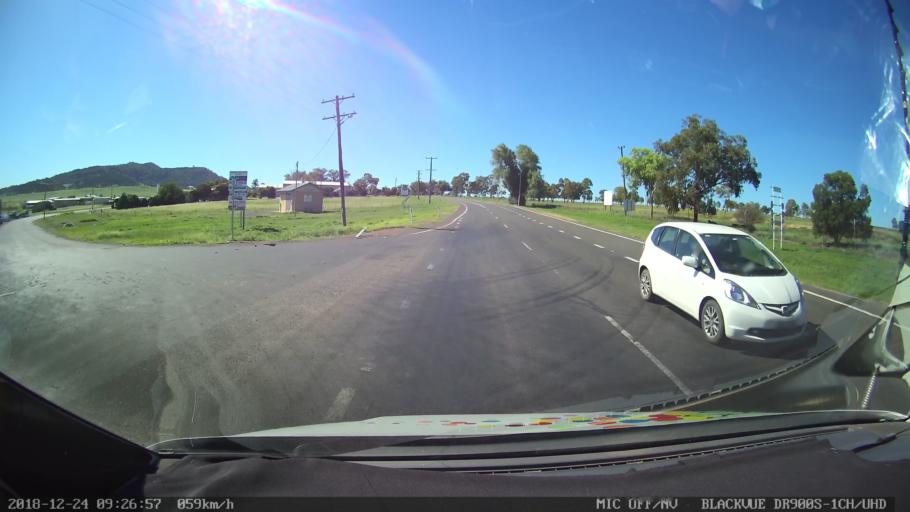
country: AU
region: New South Wales
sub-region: Liverpool Plains
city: Quirindi
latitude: -31.5238
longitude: 150.6786
